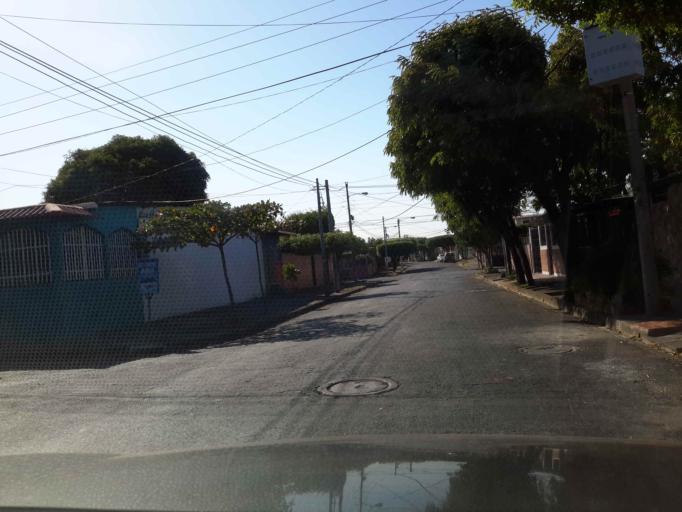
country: NI
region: Managua
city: Managua
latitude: 12.1352
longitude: -86.2449
